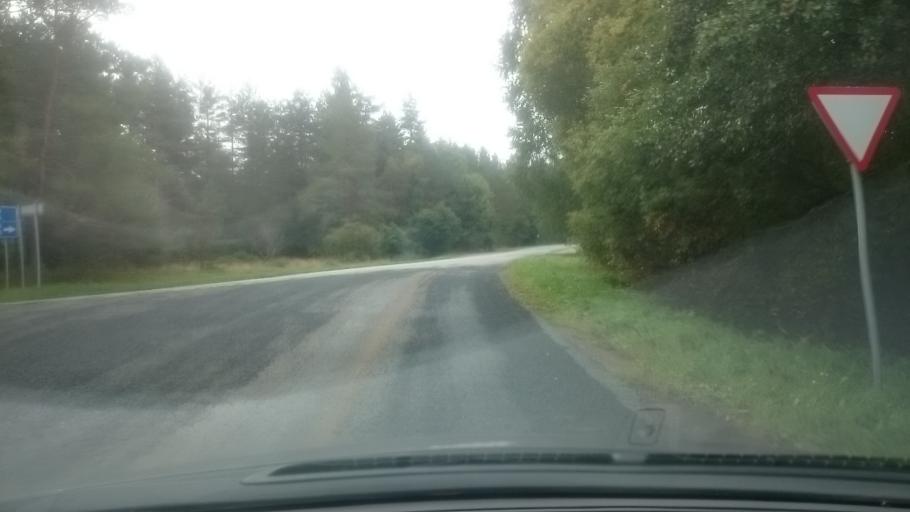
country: EE
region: Harju
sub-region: Raasiku vald
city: Raasiku
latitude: 59.4652
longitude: 25.2396
